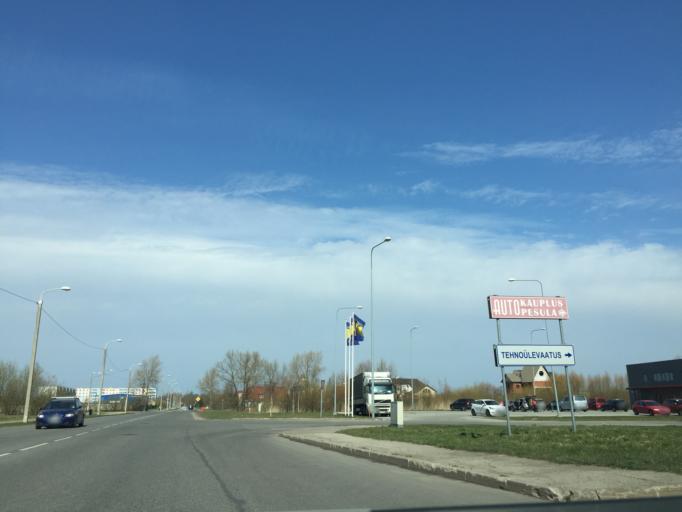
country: EE
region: Ida-Virumaa
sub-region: Narva linn
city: Narva
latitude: 59.3885
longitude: 28.1874
